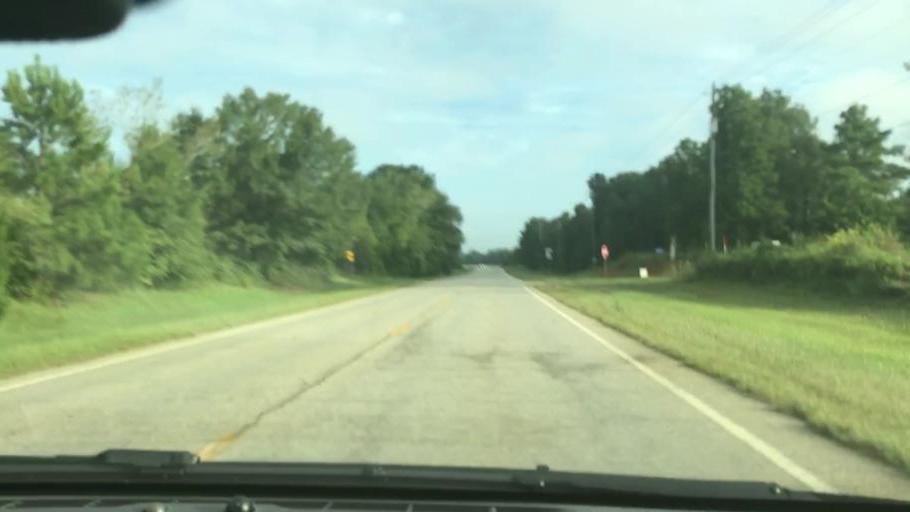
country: US
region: Georgia
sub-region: Clay County
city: Fort Gaines
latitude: 31.7321
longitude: -85.0471
